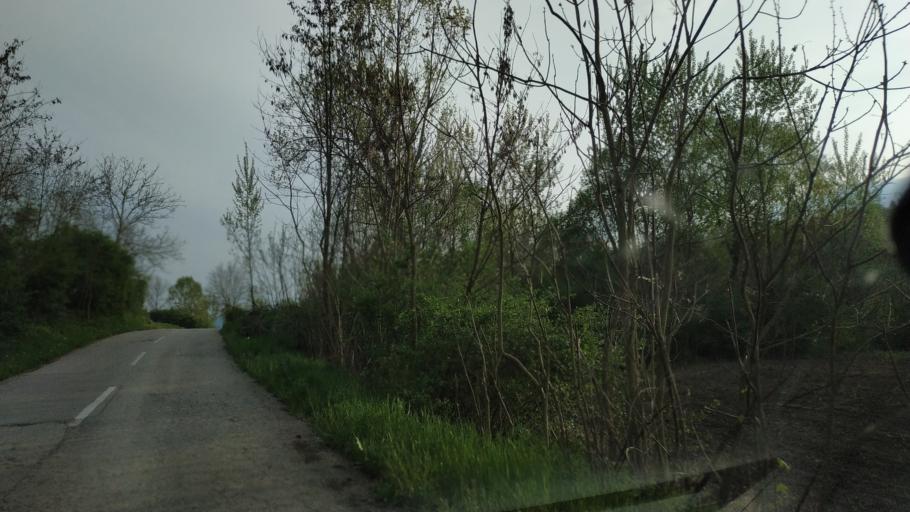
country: RS
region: Central Serbia
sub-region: Nisavski Okrug
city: Aleksinac
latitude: 43.4578
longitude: 21.8007
